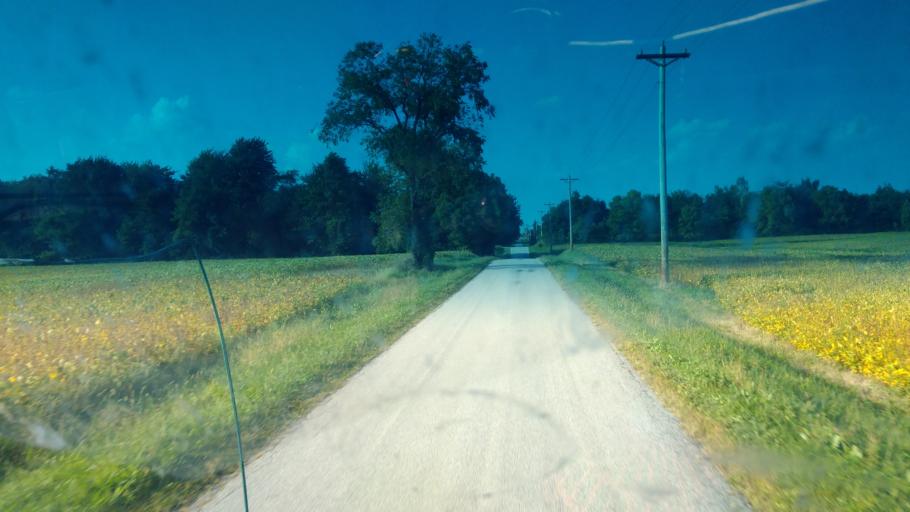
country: US
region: Ohio
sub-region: Seneca County
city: Tiffin
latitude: 40.9449
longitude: -83.1125
